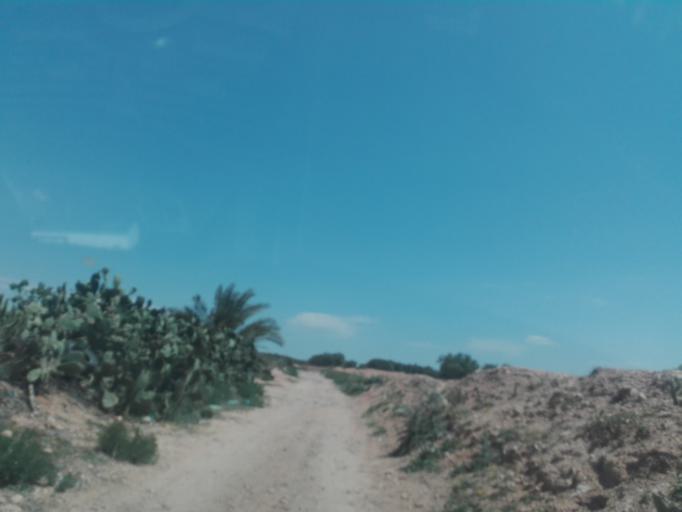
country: TN
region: Safaqis
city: Sfax
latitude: 34.6540
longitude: 10.5859
